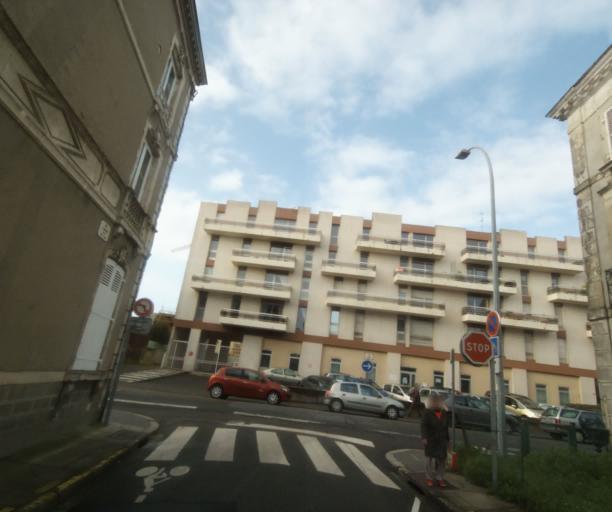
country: FR
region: Pays de la Loire
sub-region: Departement de la Sarthe
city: Le Mans
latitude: 47.9973
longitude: 0.2033
